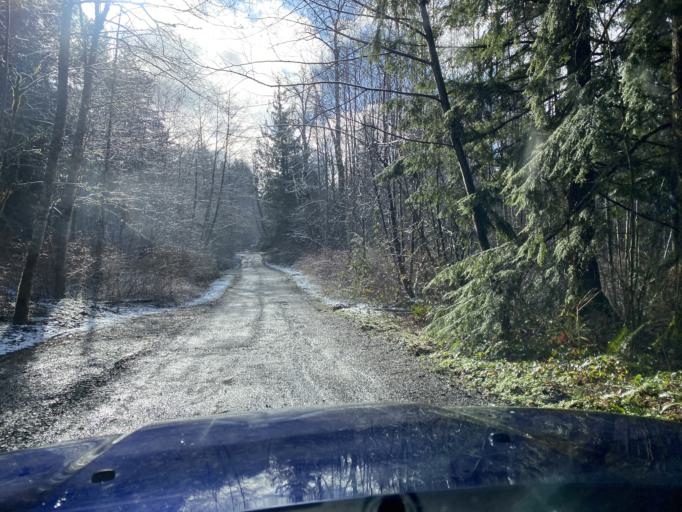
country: US
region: Washington
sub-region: King County
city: Snoqualmie
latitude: 47.5062
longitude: -121.8764
